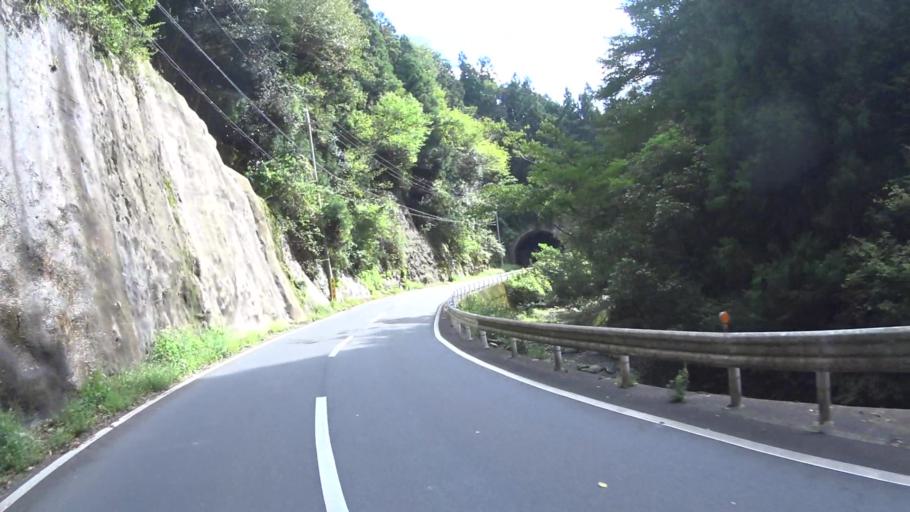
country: JP
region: Kyoto
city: Uji
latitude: 34.9202
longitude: 135.8573
